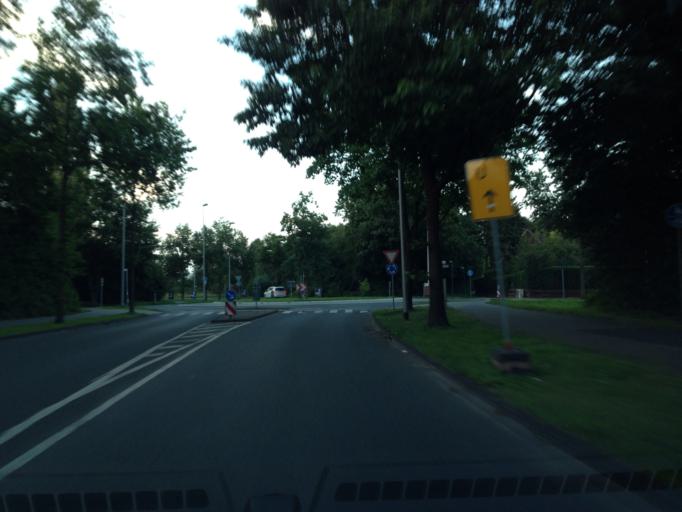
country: DE
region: North Rhine-Westphalia
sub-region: Regierungsbezirk Munster
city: Muenster
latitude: 51.9092
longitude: 7.6257
